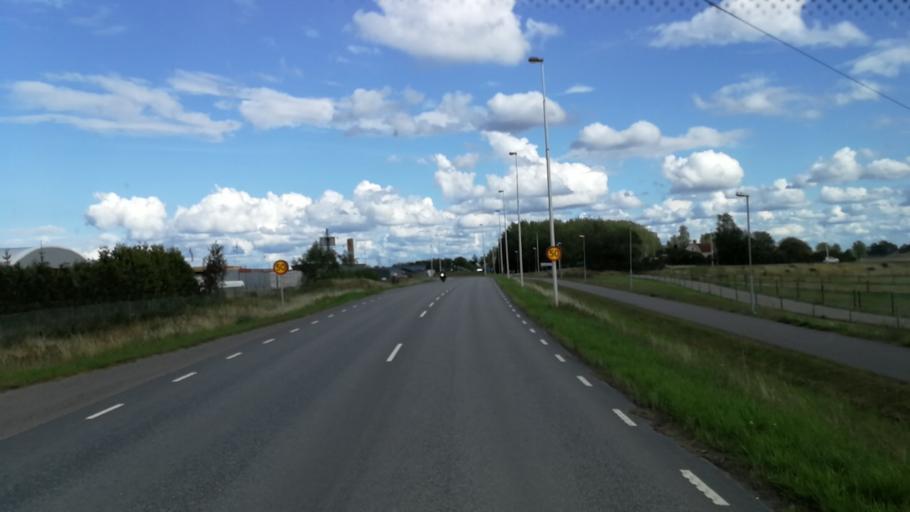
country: SE
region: OEstergoetland
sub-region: Linkopings Kommun
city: Ljungsbro
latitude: 58.4907
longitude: 15.4949
